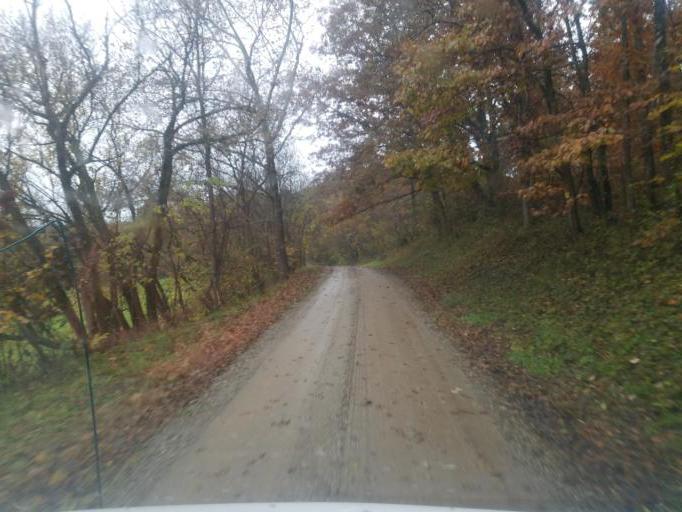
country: US
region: Ohio
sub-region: Washington County
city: Beverly
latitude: 39.4587
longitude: -81.7746
